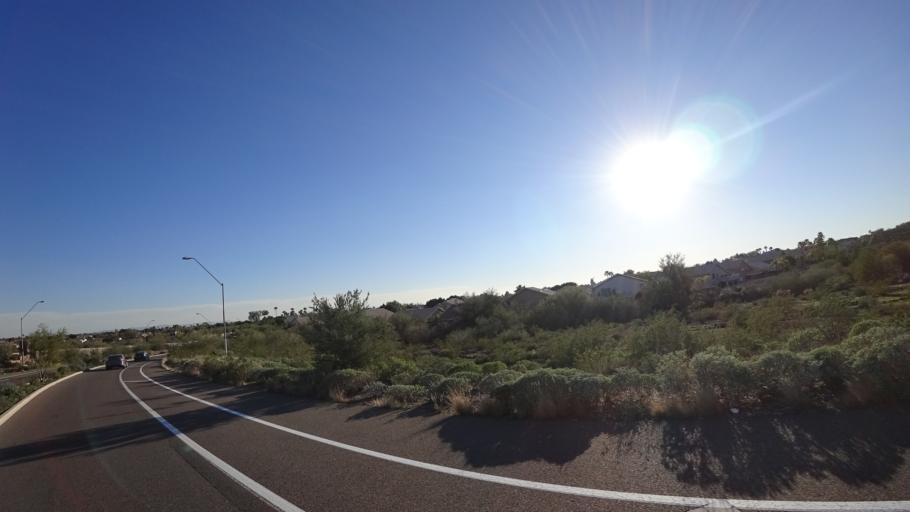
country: US
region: Arizona
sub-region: Maricopa County
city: Peoria
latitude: 33.6874
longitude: -112.1870
